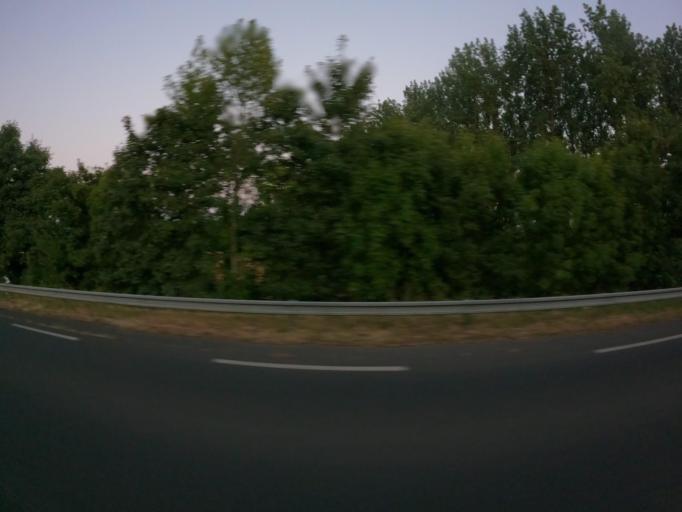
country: FR
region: Pays de la Loire
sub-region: Departement de Maine-et-Loire
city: Cande
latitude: 47.5363
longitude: -1.0753
